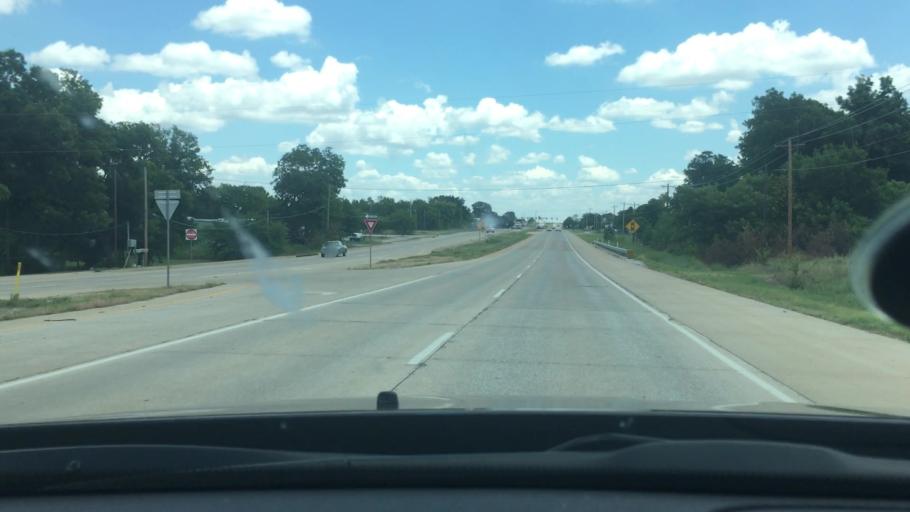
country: US
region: Oklahoma
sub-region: Carter County
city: Lone Grove
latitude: 34.1728
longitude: -97.2361
